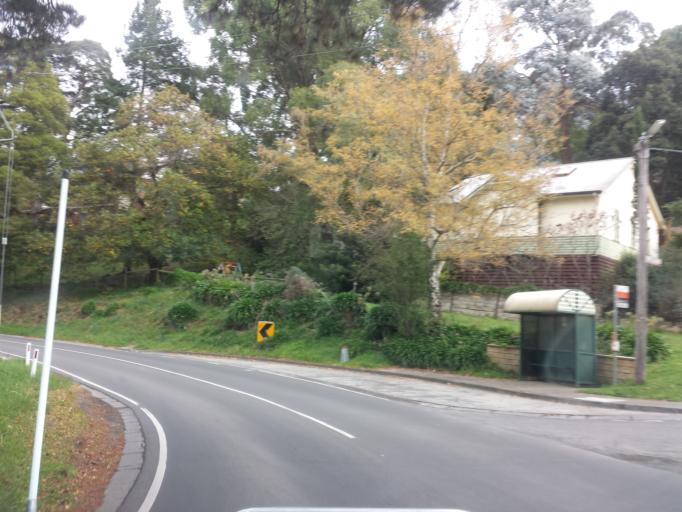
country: AU
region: Victoria
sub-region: Yarra Ranges
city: Monbulk
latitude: -37.8857
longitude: 145.3921
